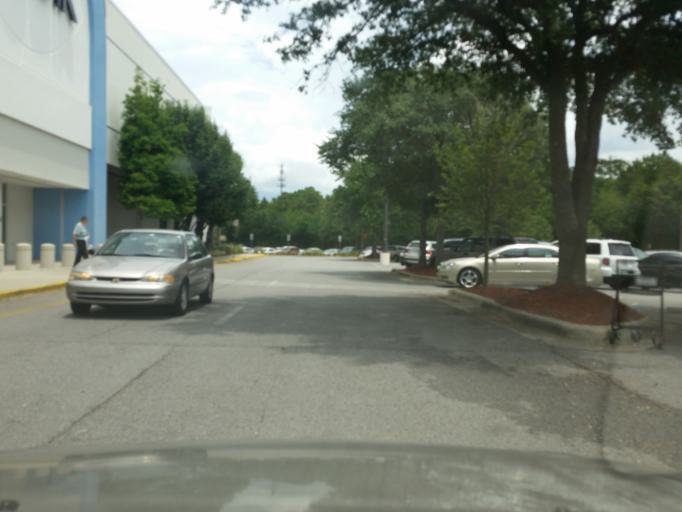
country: US
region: Florida
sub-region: Escambia County
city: Brent
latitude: 30.4738
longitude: -87.2065
